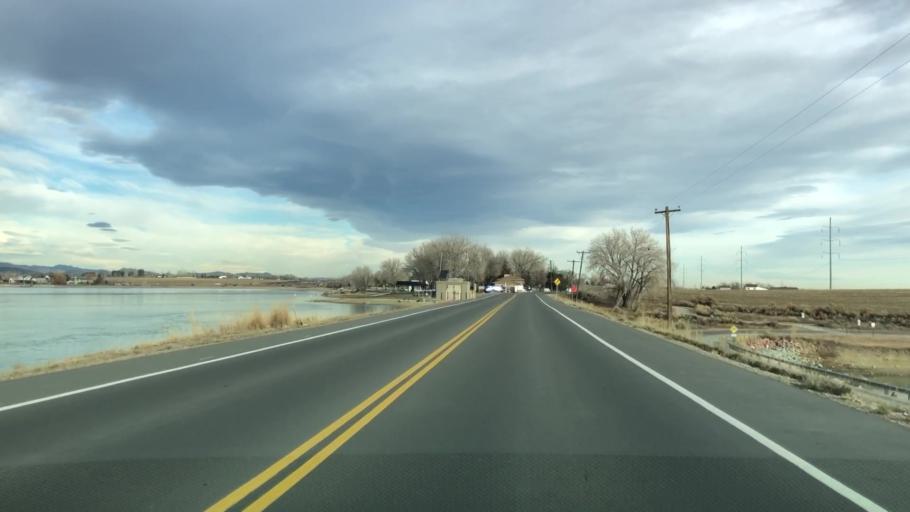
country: US
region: Colorado
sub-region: Larimer County
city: Loveland
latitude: 40.4398
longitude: -105.0456
